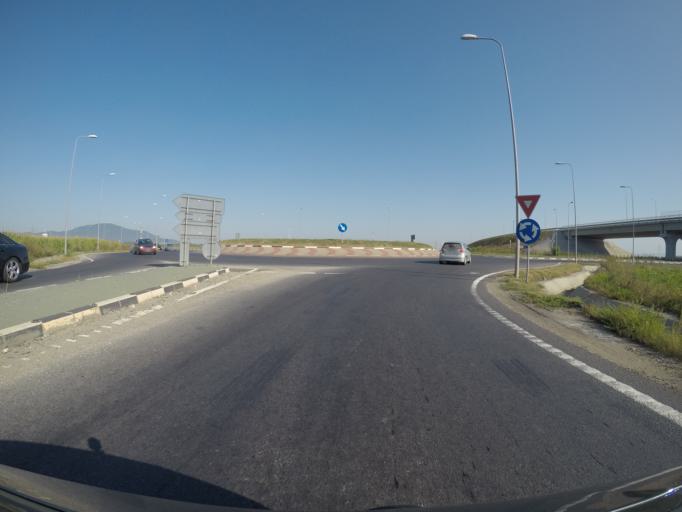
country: RO
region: Brasov
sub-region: Comuna Ghimbav
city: Ghimbav
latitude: 45.6615
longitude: 25.5339
